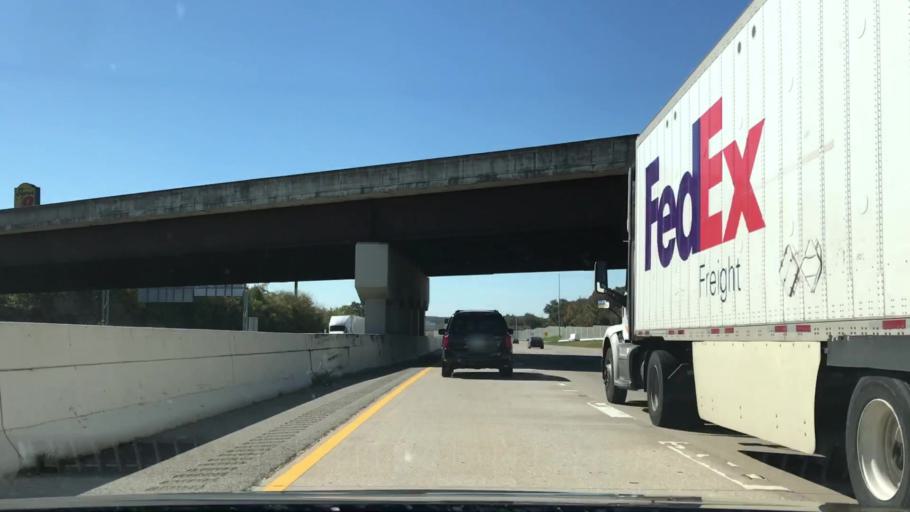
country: US
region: Tennessee
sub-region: Davidson County
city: Nashville
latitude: 36.2378
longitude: -86.7575
